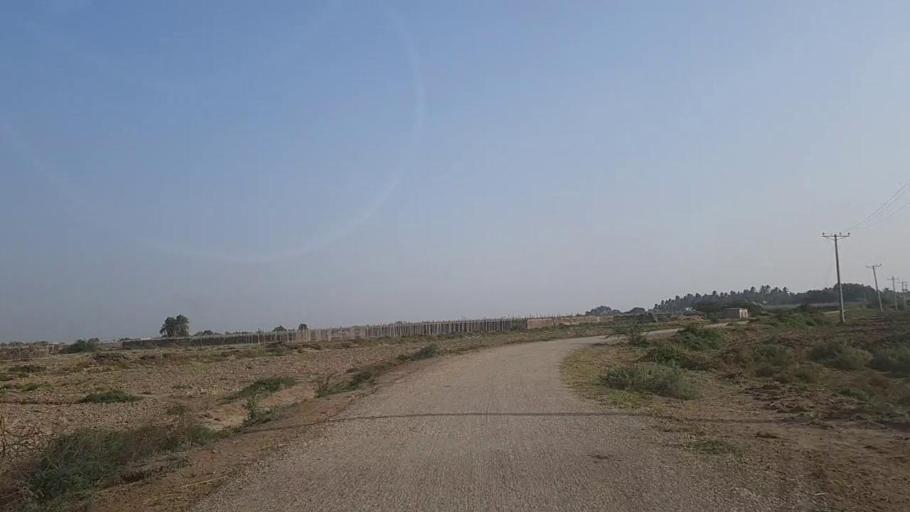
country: PK
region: Sindh
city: Keti Bandar
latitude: 24.1693
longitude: 67.6257
